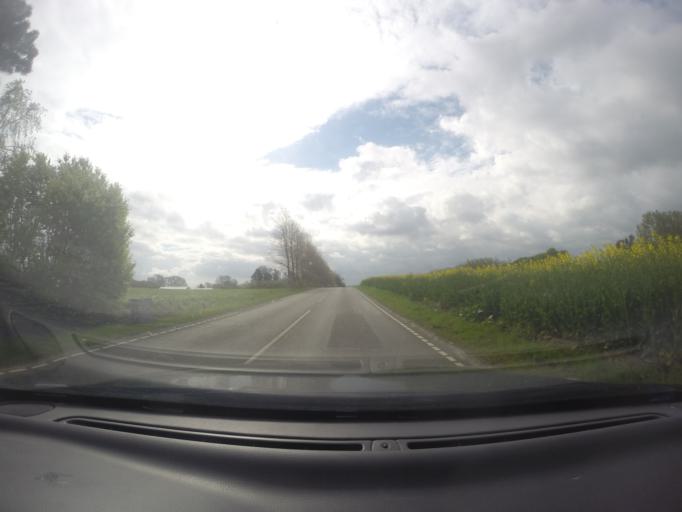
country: DK
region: Capital Region
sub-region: Hoje-Taastrup Kommune
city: Taastrup
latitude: 55.6802
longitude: 12.3091
